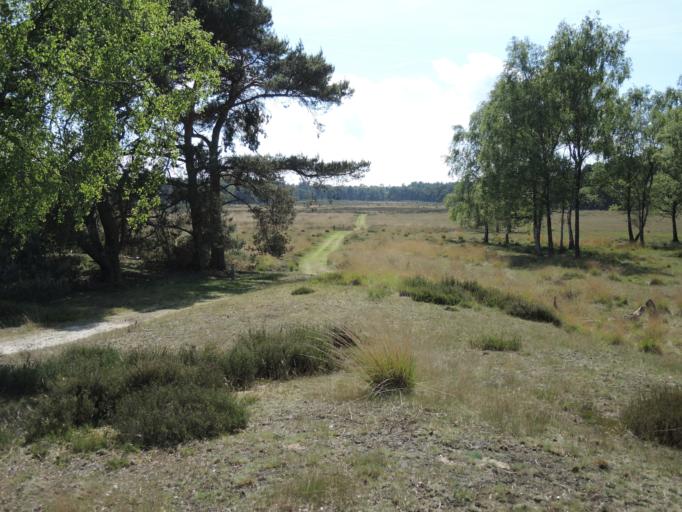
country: BE
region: Flanders
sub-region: Provincie Antwerpen
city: Kalmthout
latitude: 51.3910
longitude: 4.4289
